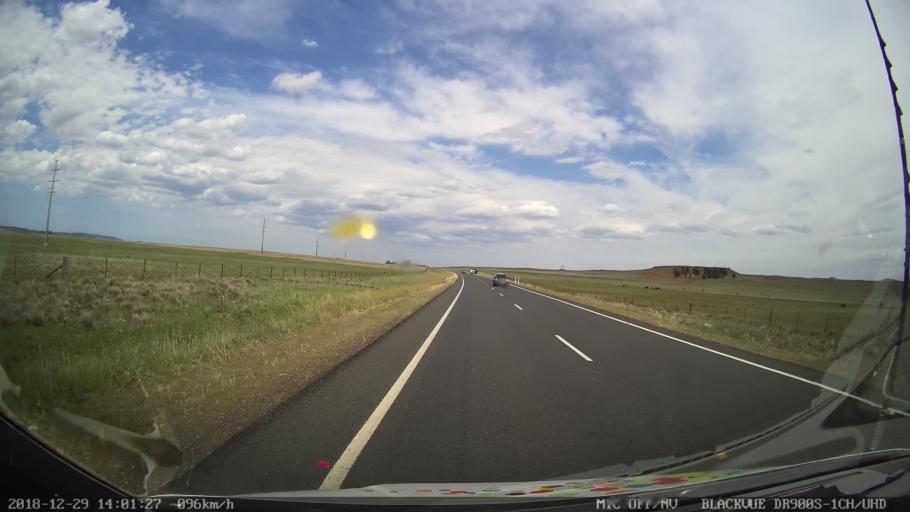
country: AU
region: New South Wales
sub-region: Cooma-Monaro
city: Cooma
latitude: -36.2755
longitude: 149.1680
